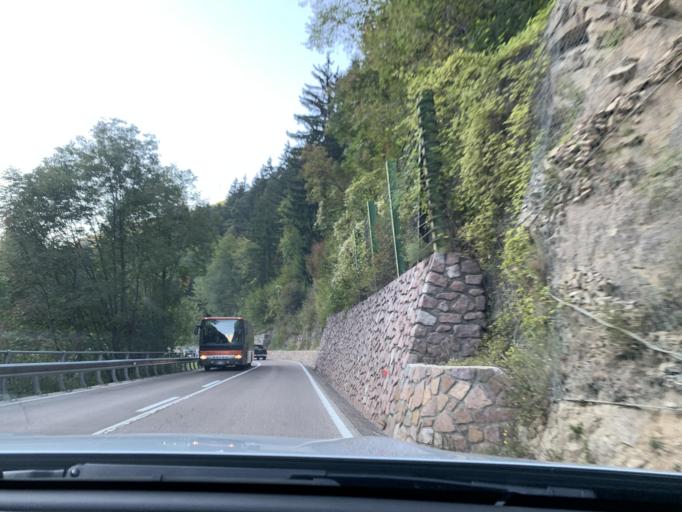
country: IT
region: Trentino-Alto Adige
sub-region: Bolzano
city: Nova Ponente
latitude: 46.4504
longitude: 11.4479
